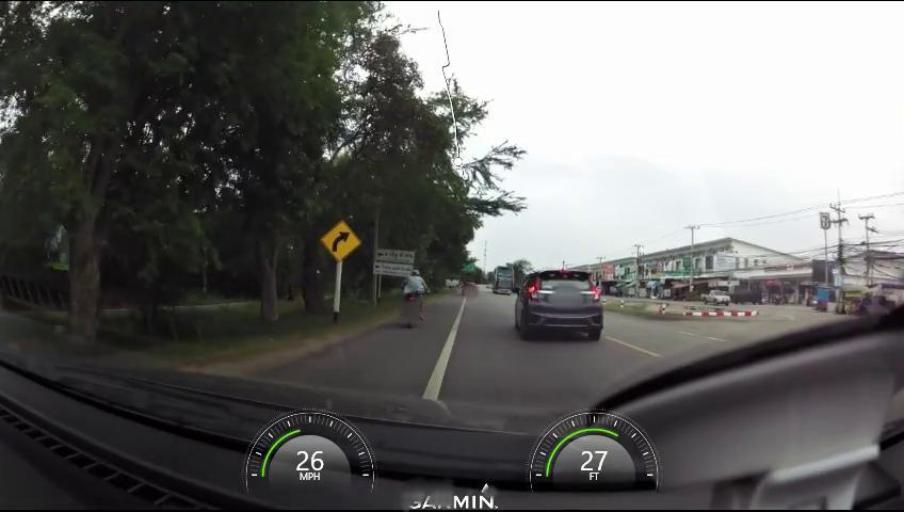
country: TH
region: Prachuap Khiri Khan
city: Hua Hin
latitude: 12.4712
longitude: 99.9716
